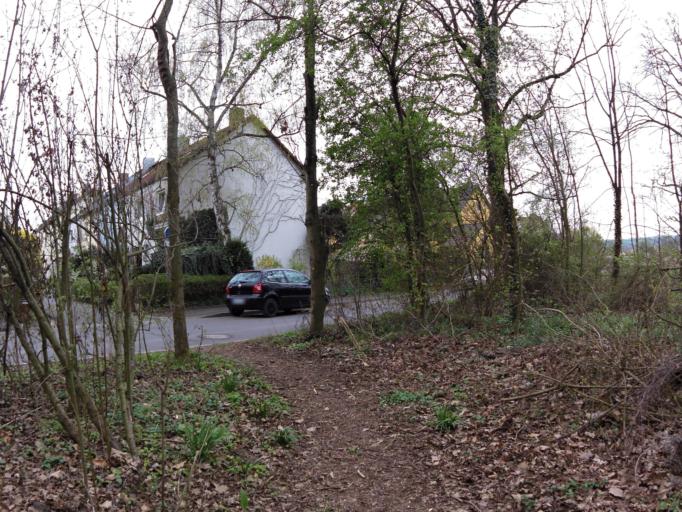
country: DE
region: Bavaria
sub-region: Regierungsbezirk Unterfranken
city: Rottendorf
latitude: 49.7970
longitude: 10.0191
